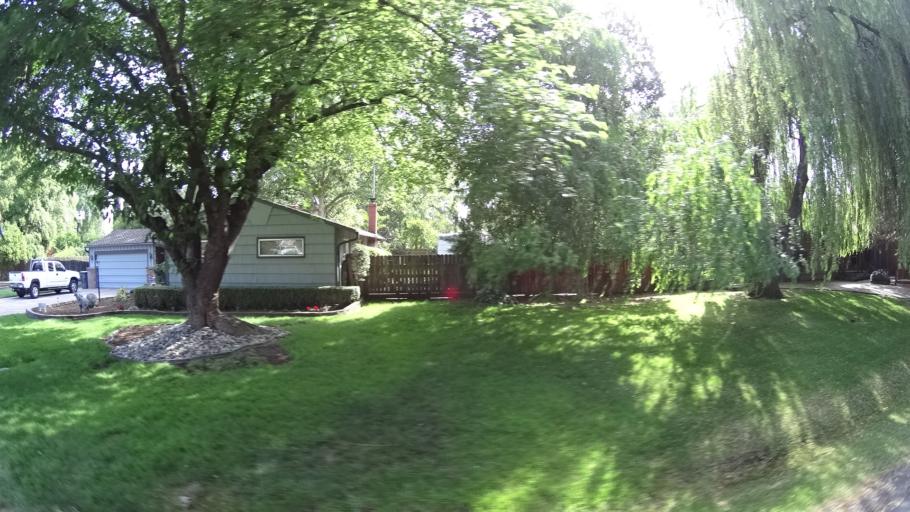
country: US
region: California
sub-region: Sacramento County
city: Parkway
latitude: 38.4840
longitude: -121.5101
